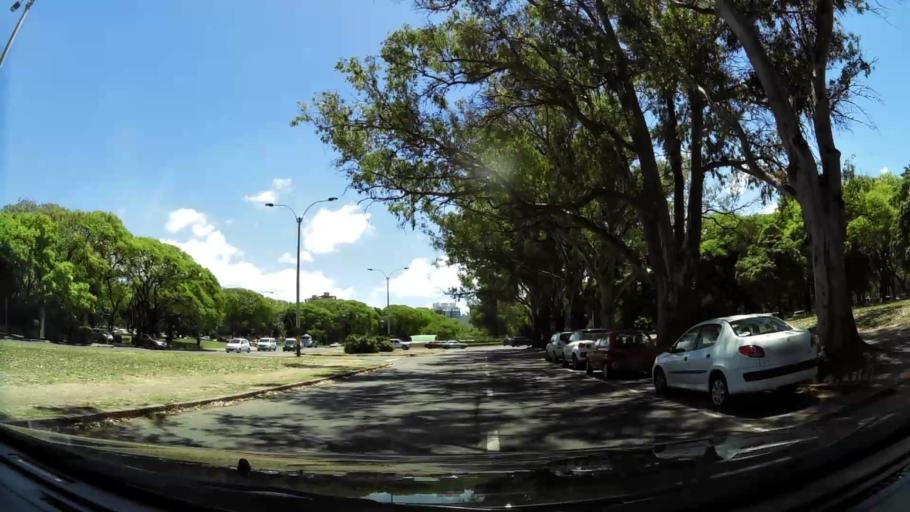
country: UY
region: Montevideo
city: Montevideo
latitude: -34.8967
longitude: -56.1590
